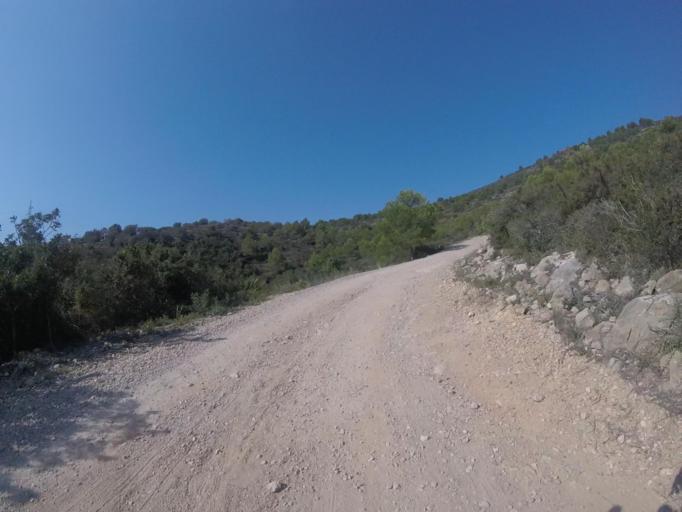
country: ES
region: Valencia
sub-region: Provincia de Castello
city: Peniscola
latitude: 40.3285
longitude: 0.3552
